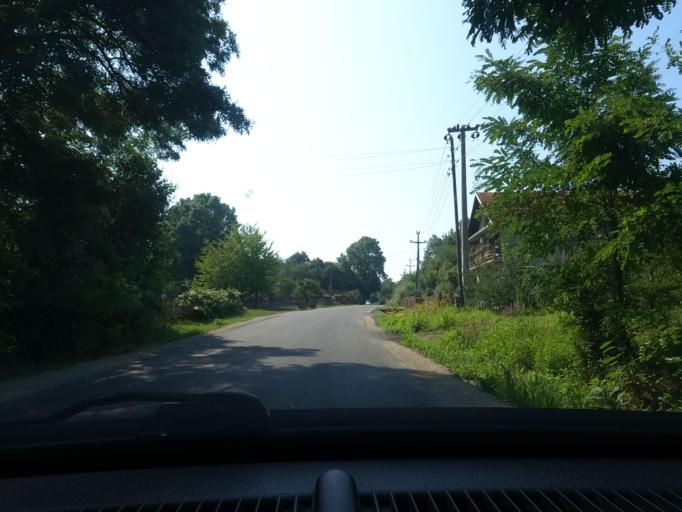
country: RS
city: Kozjak
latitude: 44.5644
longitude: 19.2897
